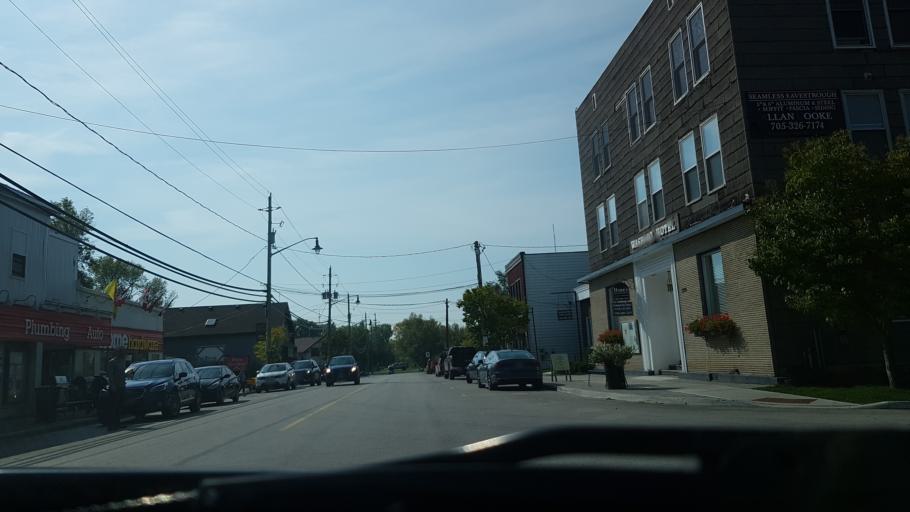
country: CA
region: Ontario
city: Orillia
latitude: 44.7510
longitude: -79.3334
